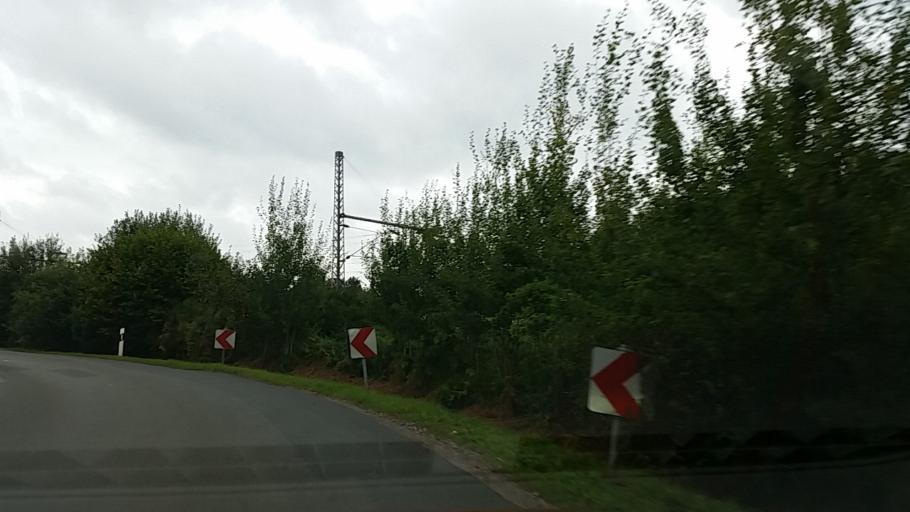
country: DE
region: North Rhine-Westphalia
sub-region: Regierungsbezirk Munster
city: Lotte
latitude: 52.2924
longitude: 7.9317
